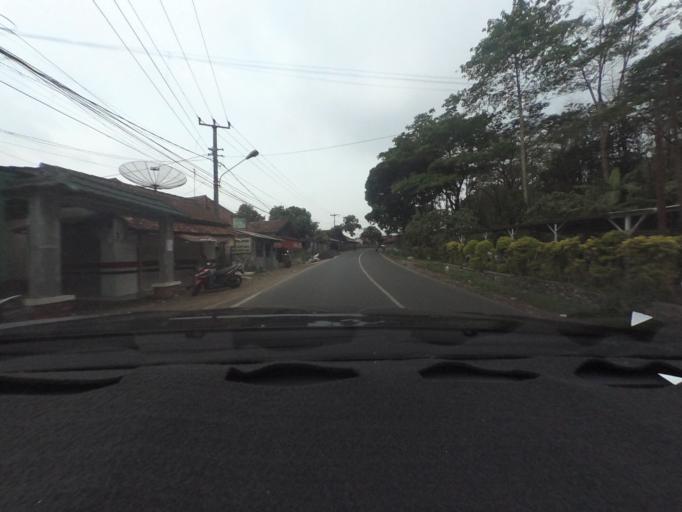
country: ID
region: West Java
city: Cicurug
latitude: -6.8072
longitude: 106.7694
